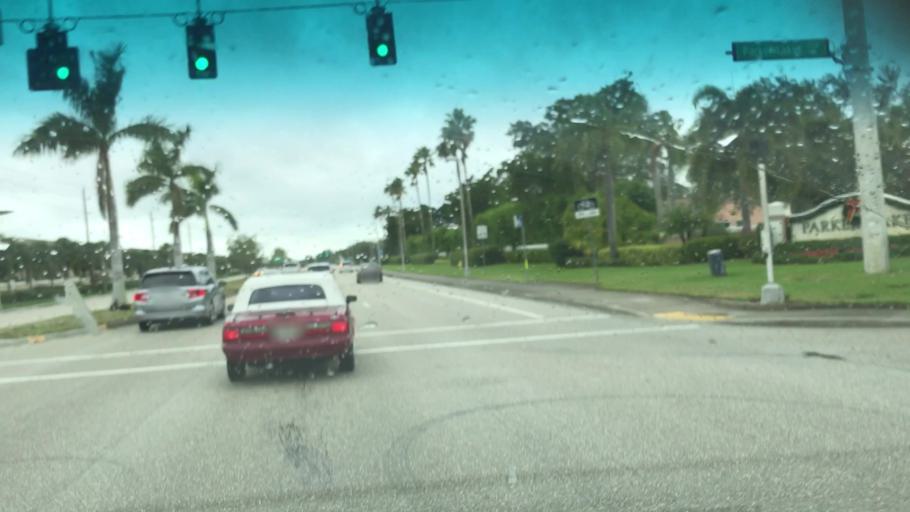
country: US
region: Florida
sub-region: Lee County
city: Cypress Lake
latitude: 26.5205
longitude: -81.9068
